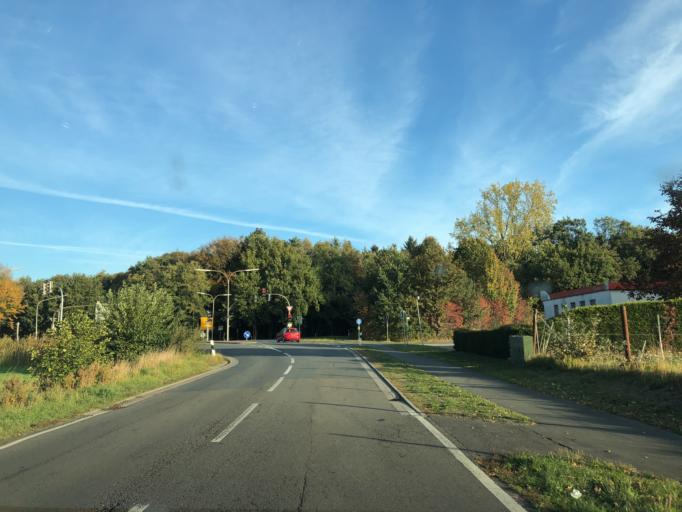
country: DE
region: Lower Saxony
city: Lehe
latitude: 53.0488
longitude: 7.3454
